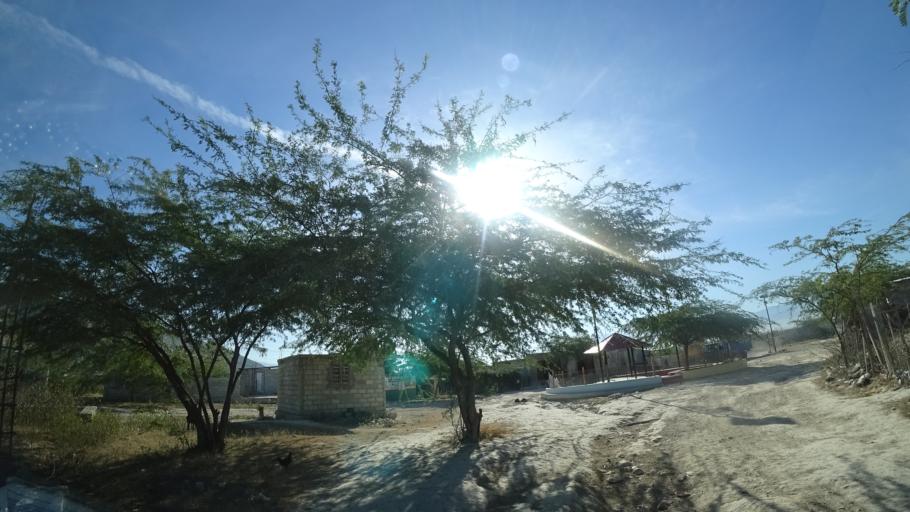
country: HT
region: Ouest
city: Croix des Bouquets
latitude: 18.6639
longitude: -72.2326
